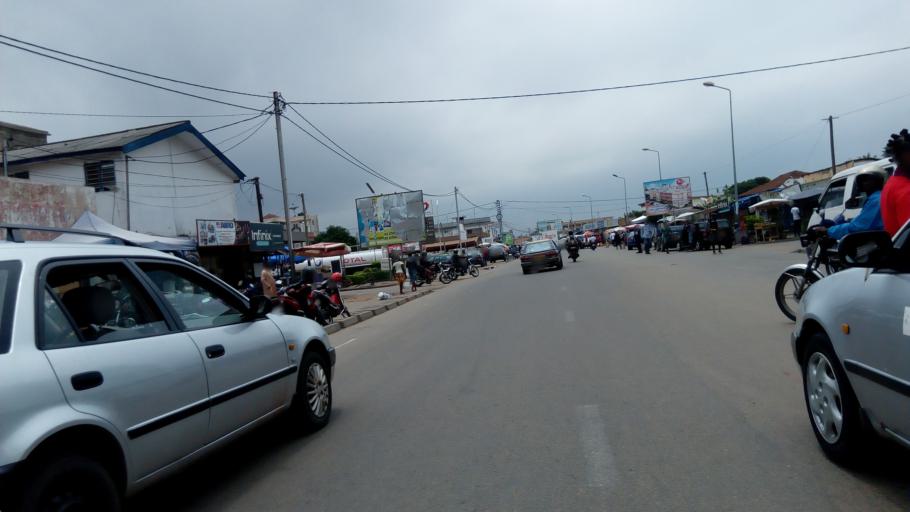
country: TG
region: Maritime
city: Lome
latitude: 6.1379
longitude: 1.2293
